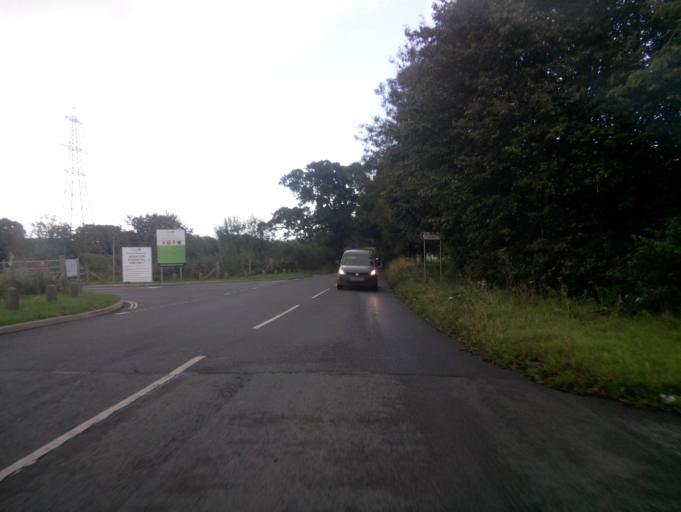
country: GB
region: England
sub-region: Devon
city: Ivybridge
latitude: 50.3835
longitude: -3.9239
